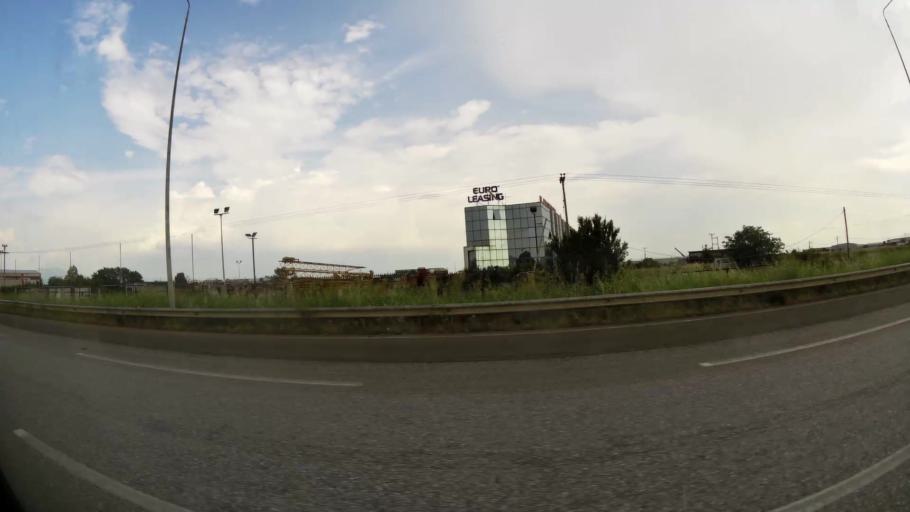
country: GR
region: Central Macedonia
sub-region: Nomos Thessalonikis
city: Sindos
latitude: 40.6512
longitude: 22.8192
